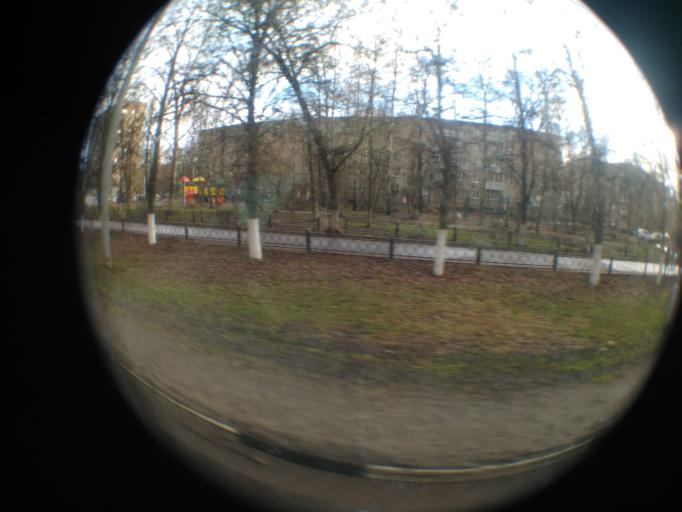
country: RU
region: Moskovskaya
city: Il'inskiy
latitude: 55.6056
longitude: 38.1001
